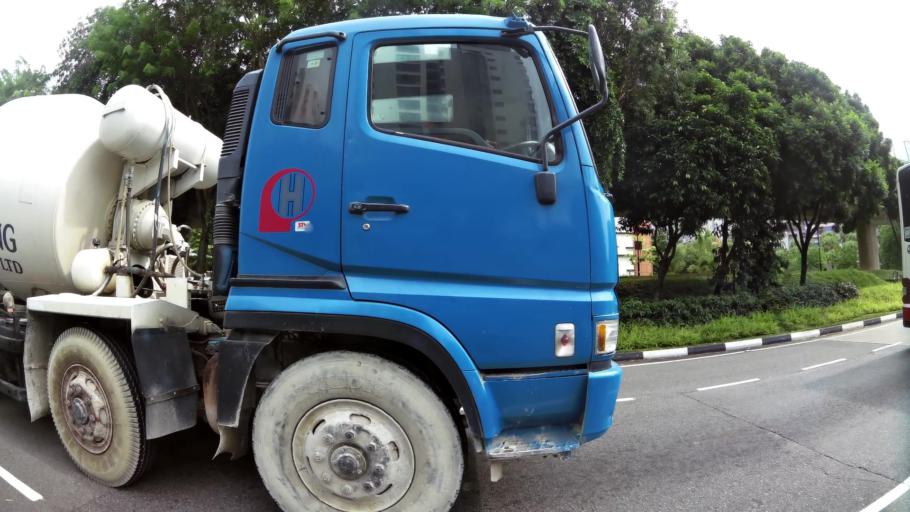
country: MY
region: Johor
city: Johor Bahru
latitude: 1.4428
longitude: 103.8052
